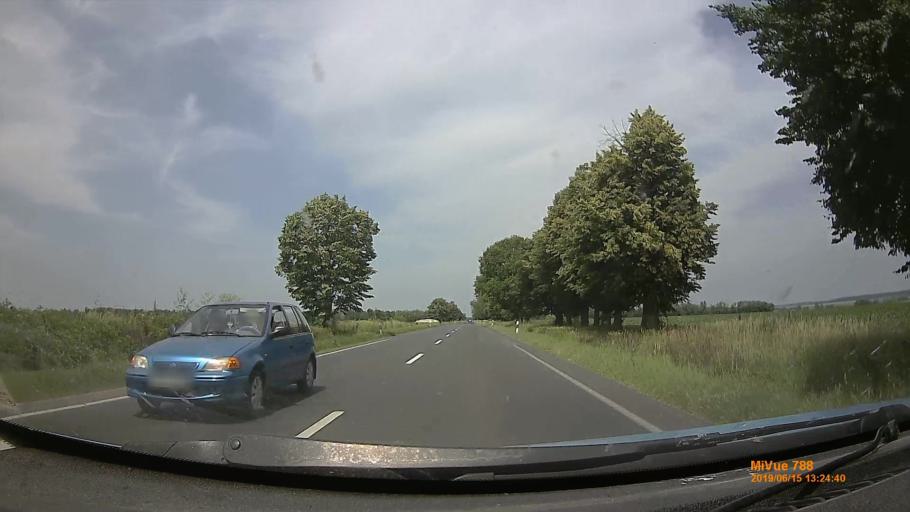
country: HU
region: Tolna
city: Dobrokoz
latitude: 46.4798
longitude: 18.1590
